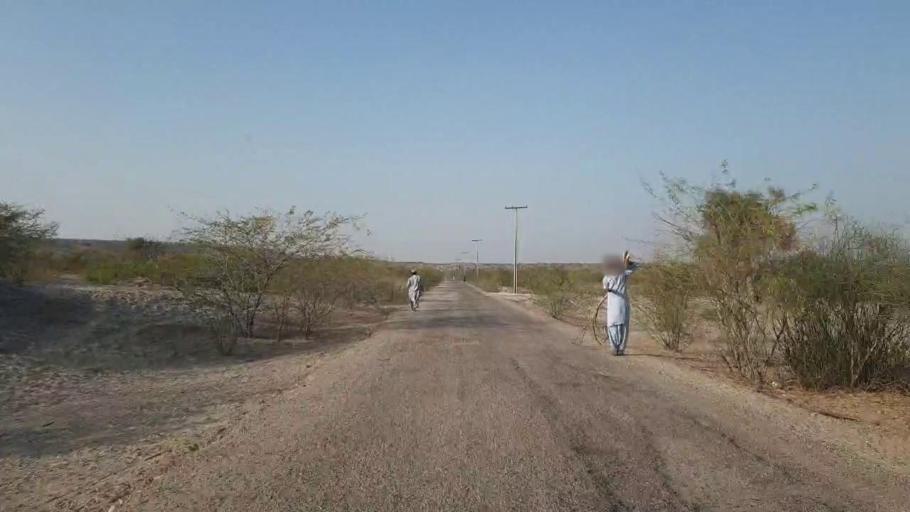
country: PK
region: Sindh
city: Chor
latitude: 25.5955
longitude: 69.8380
